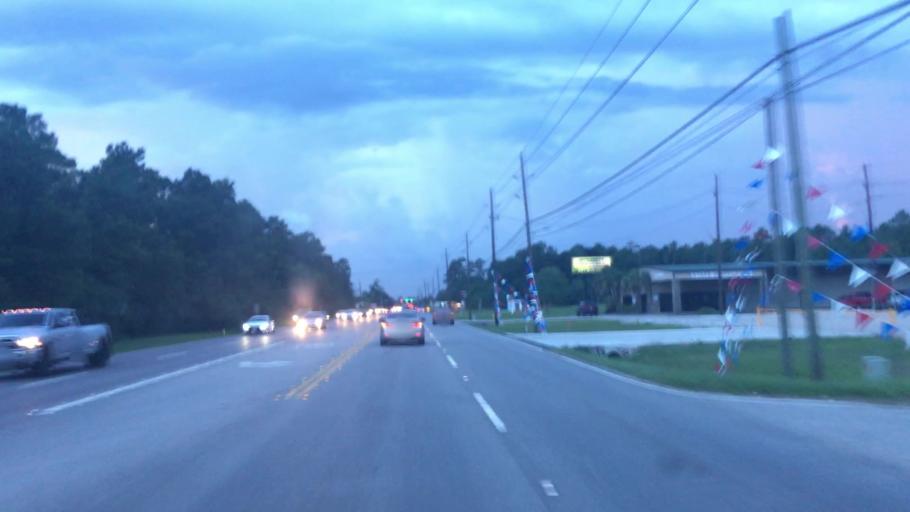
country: US
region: Texas
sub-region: Harris County
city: Atascocita
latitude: 29.9862
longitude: -95.1995
